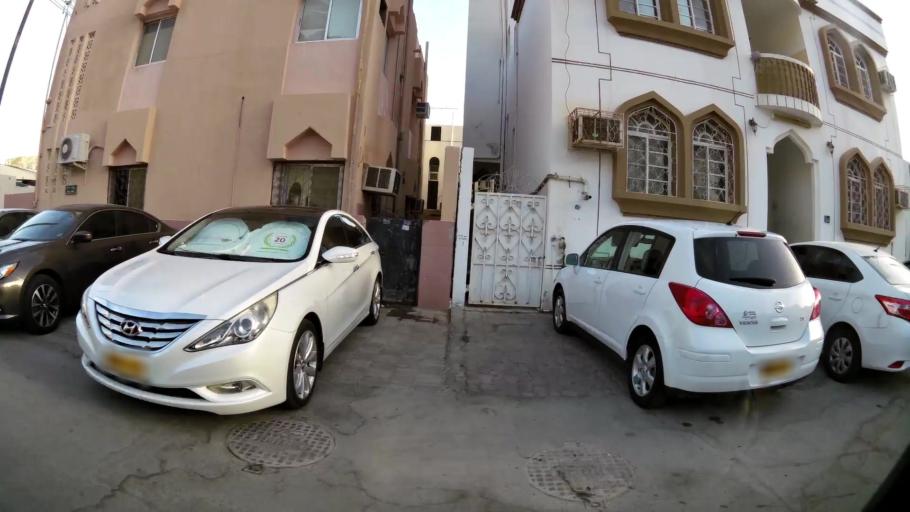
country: OM
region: Muhafazat Masqat
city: Muscat
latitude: 23.5764
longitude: 58.5753
